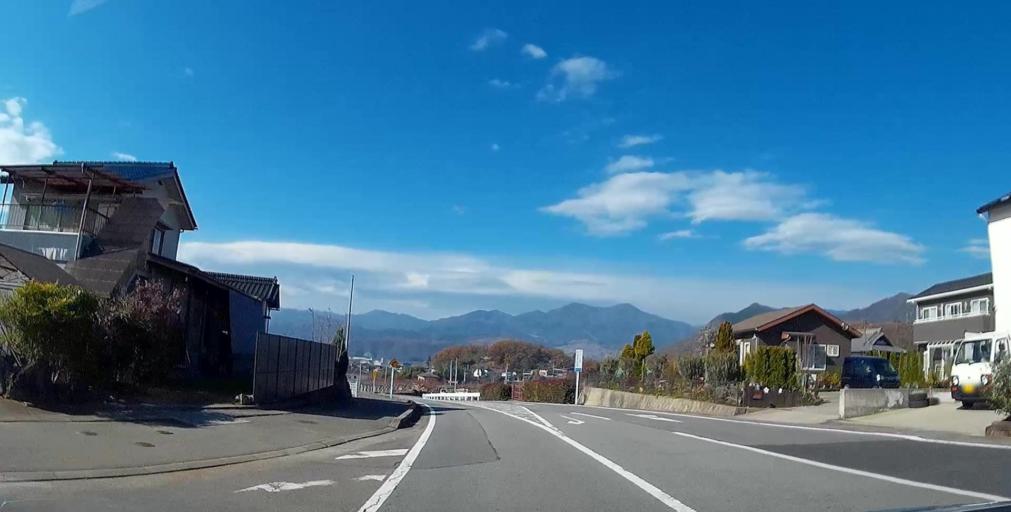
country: JP
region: Yamanashi
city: Enzan
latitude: 35.7135
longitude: 138.7444
